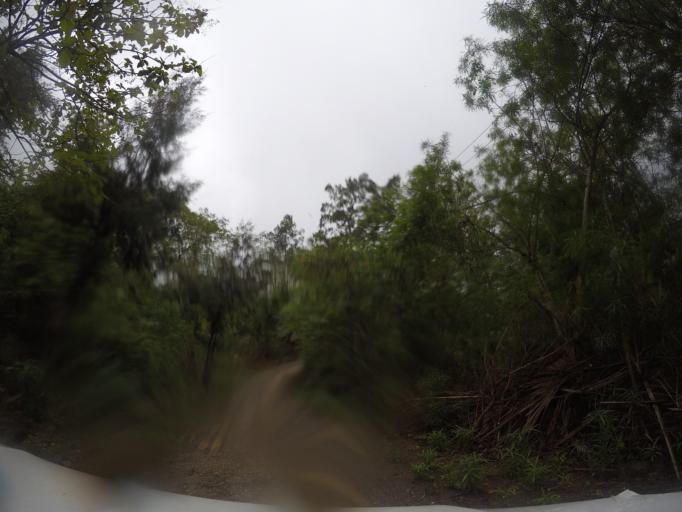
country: TL
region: Baucau
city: Venilale
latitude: -8.6435
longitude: 126.4344
